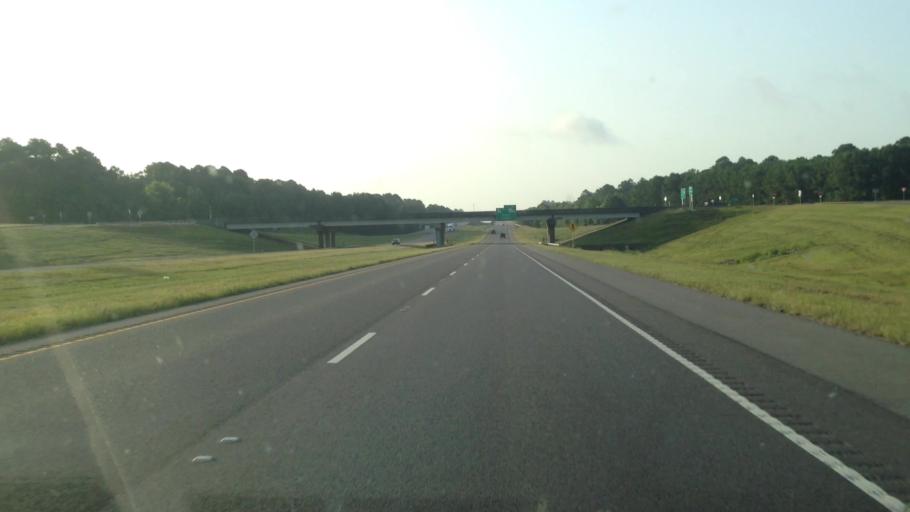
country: US
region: Louisiana
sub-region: Rapides Parish
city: Boyce
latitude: 31.4107
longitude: -92.7189
